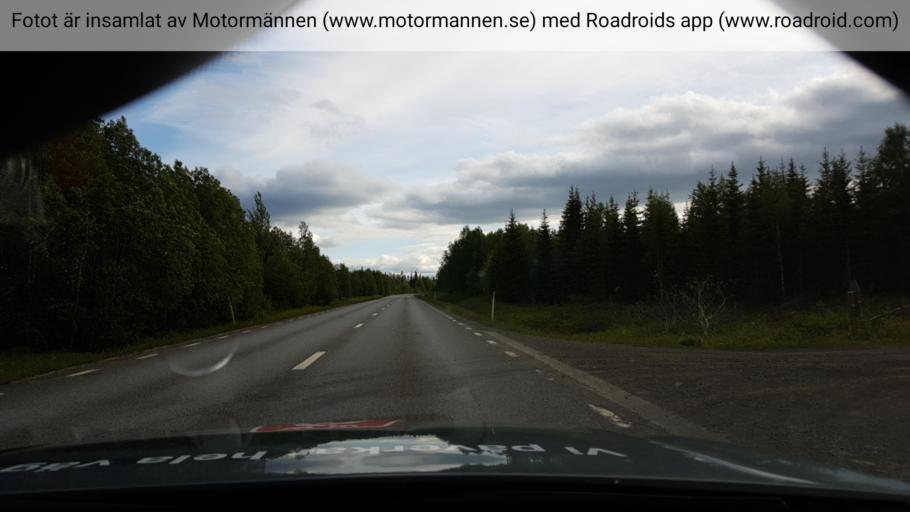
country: SE
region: Jaemtland
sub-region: OEstersunds Kommun
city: Lit
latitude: 63.4674
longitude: 15.1868
